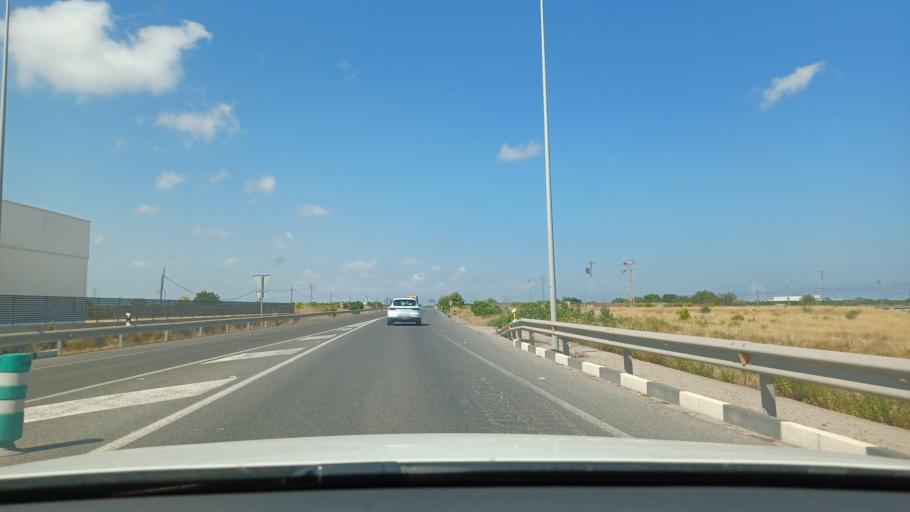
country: ES
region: Valencia
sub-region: Provincia de Castello
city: Chilches
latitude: 39.8032
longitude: -0.1748
